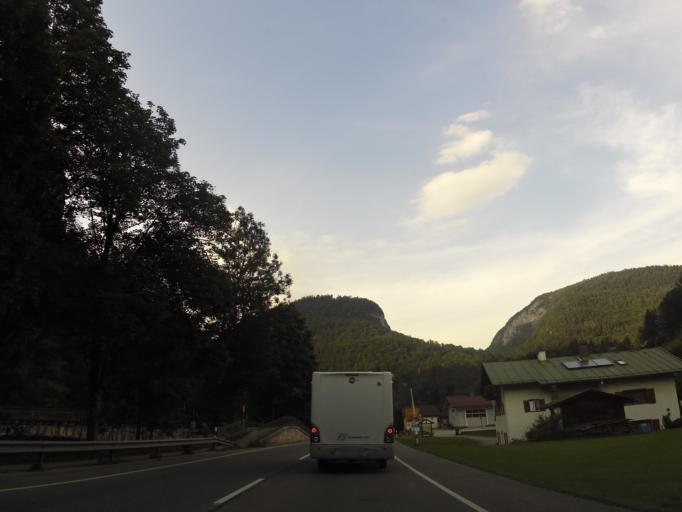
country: DE
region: Bavaria
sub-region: Upper Bavaria
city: Berchtesgaden
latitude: 47.6512
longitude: 13.0368
